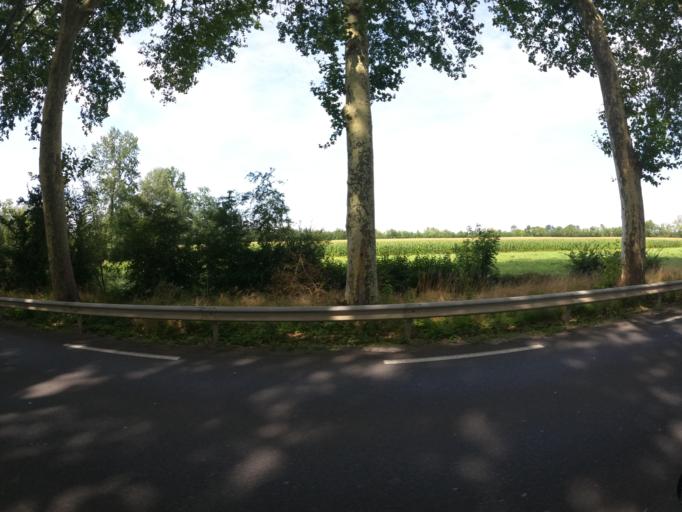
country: FR
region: Poitou-Charentes
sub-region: Departement des Deux-Sevres
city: Frontenay-Rohan-Rohan
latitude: 46.2734
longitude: -0.5263
